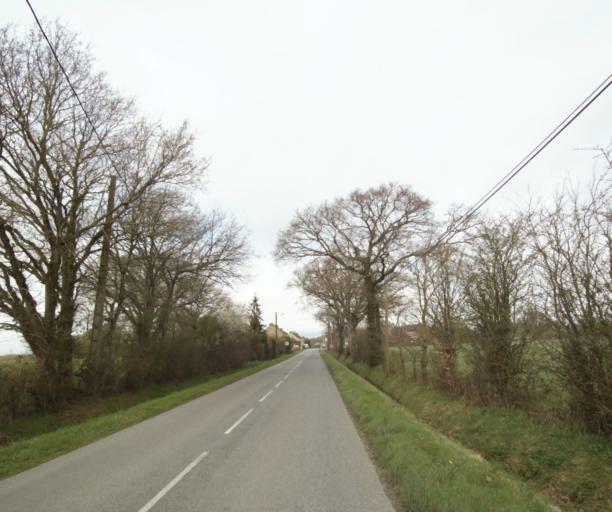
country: FR
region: Pays de la Loire
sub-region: Departement de la Loire-Atlantique
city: Bouvron
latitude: 47.4237
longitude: -1.8980
